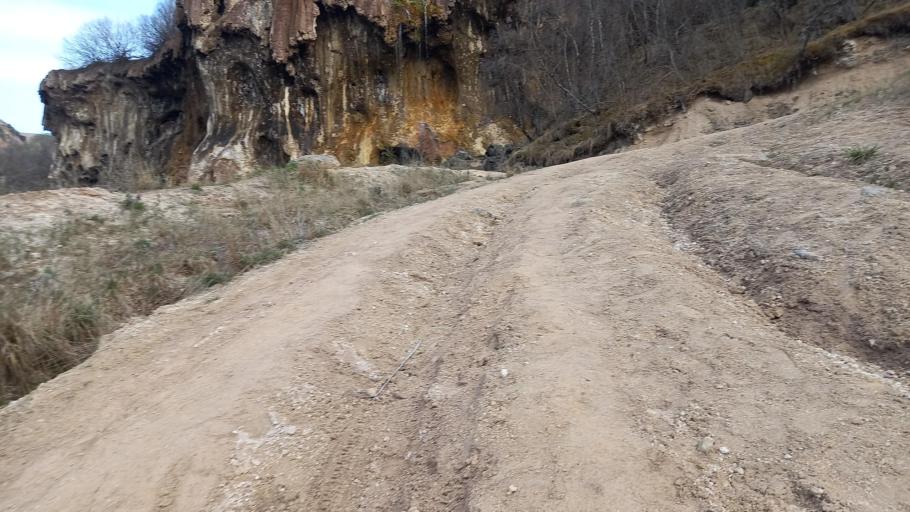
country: RU
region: Kabardino-Balkariya
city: Kamennomostskoye
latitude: 43.6921
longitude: 42.8461
